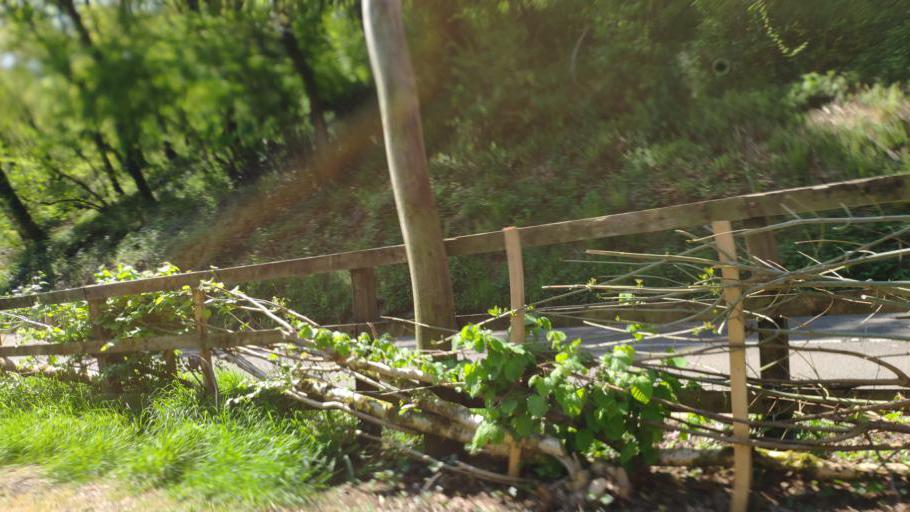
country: IE
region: Munster
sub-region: County Cork
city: Blarney
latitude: 51.9466
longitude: -8.5680
